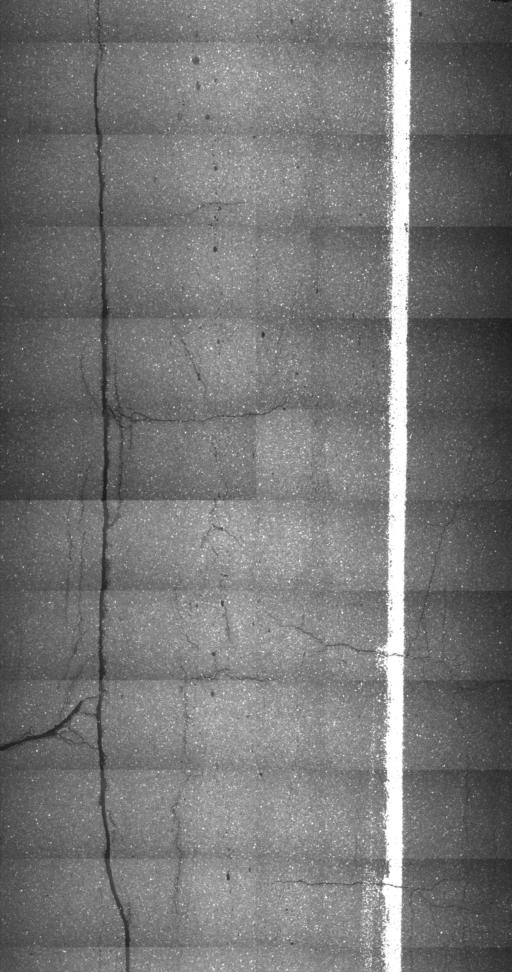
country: US
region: Vermont
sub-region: Caledonia County
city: Saint Johnsbury
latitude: 44.2982
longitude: -72.0563
